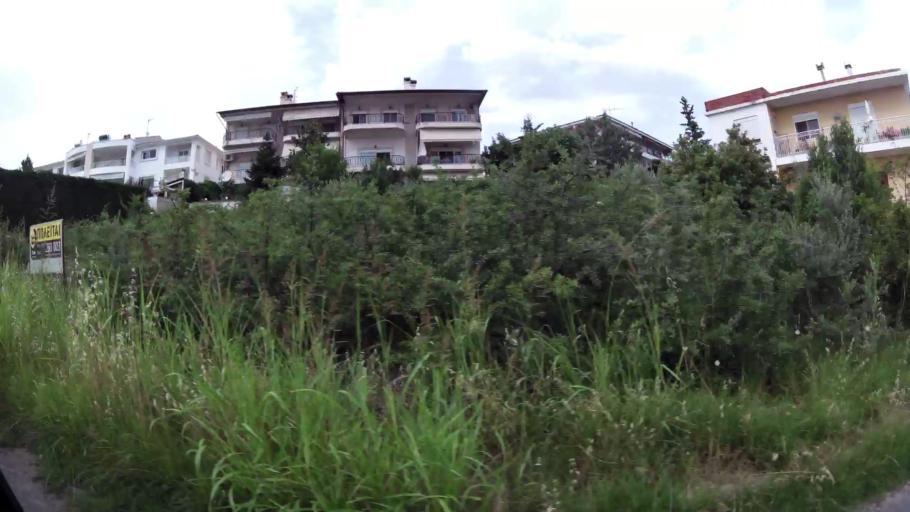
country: GR
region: Central Macedonia
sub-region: Nomos Thessalonikis
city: Oraiokastro
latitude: 40.7109
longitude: 22.9250
